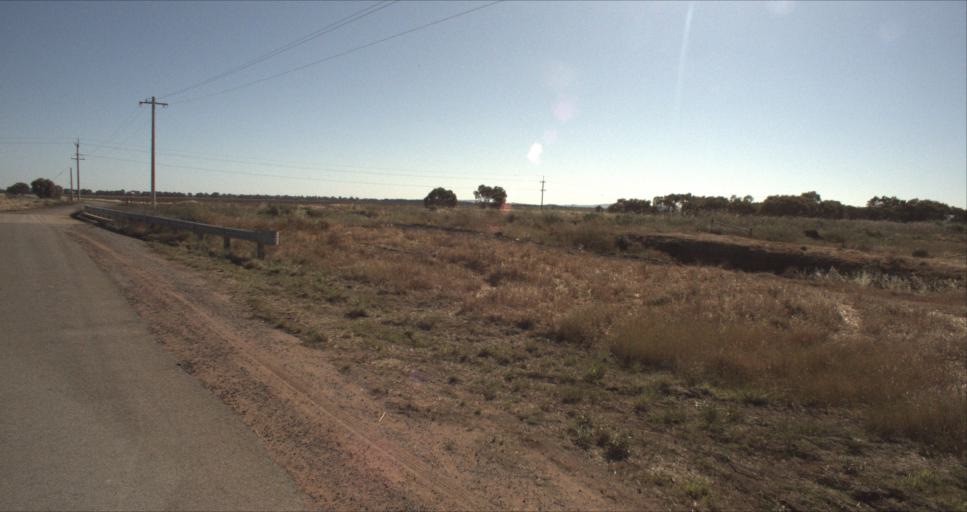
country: AU
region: New South Wales
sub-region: Leeton
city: Leeton
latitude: -34.5682
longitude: 146.3111
